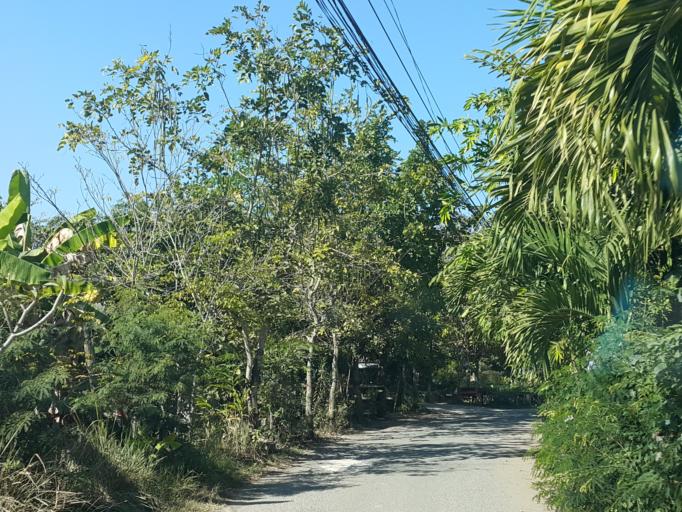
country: TH
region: Chiang Mai
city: San Sai
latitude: 18.8882
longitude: 98.9825
